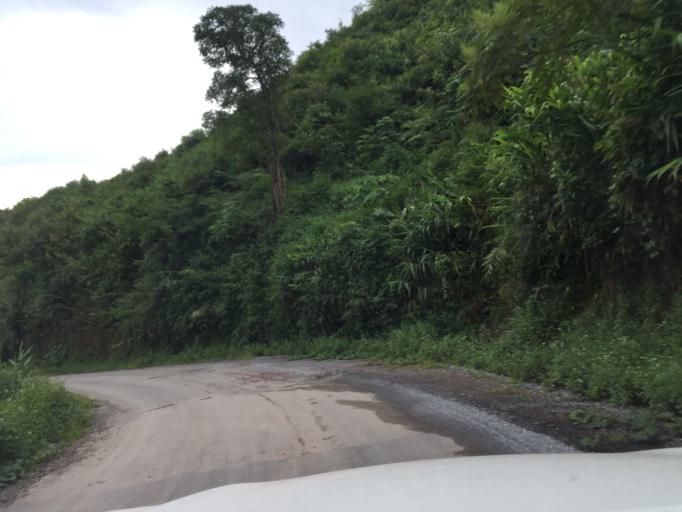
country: LA
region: Oudomxai
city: Muang La
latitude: 21.2369
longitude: 102.0747
